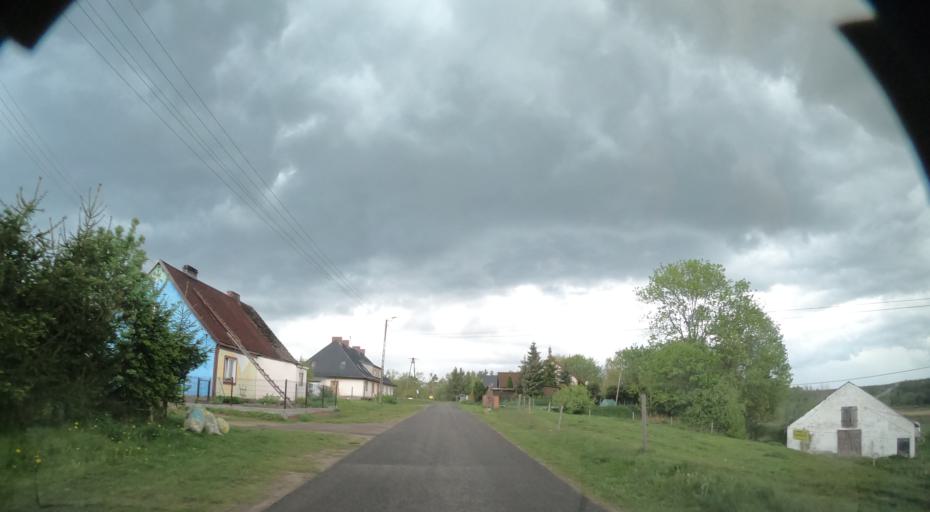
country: PL
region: West Pomeranian Voivodeship
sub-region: Powiat koszalinski
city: Bobolice
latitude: 54.1143
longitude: 16.5019
